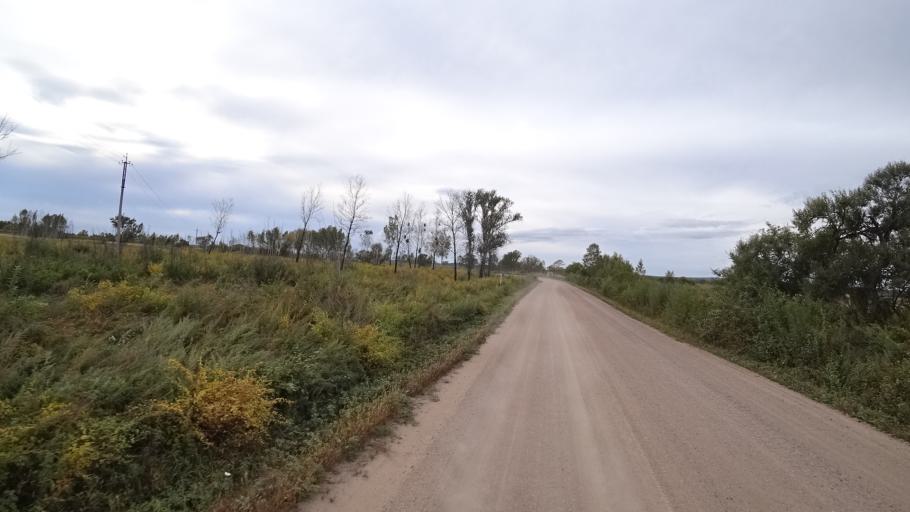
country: RU
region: Amur
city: Arkhara
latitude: 49.3779
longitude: 130.1788
